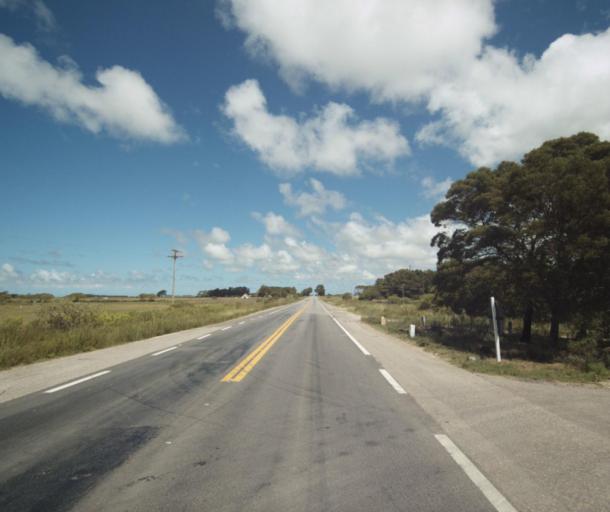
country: UY
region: Cerro Largo
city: Rio Branco
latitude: -32.8842
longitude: -52.7206
